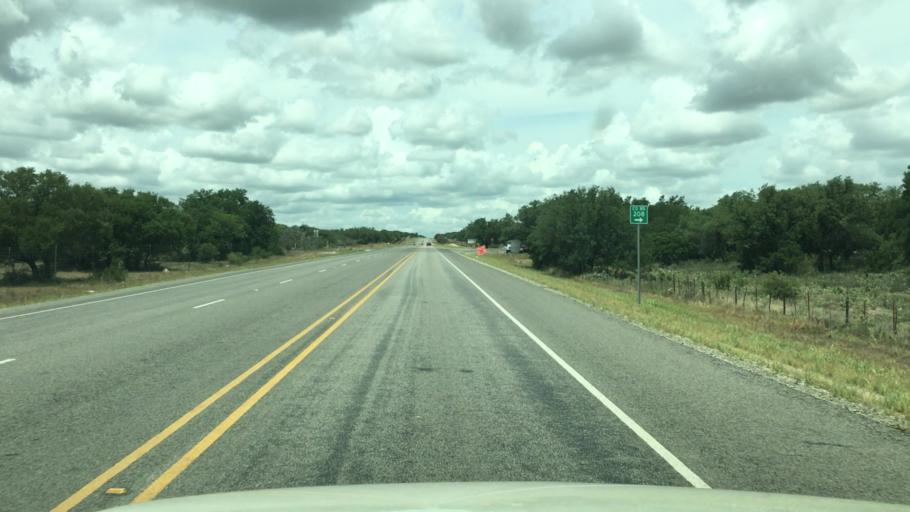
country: US
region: Texas
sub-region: McCulloch County
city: Brady
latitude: 31.0266
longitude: -99.2238
